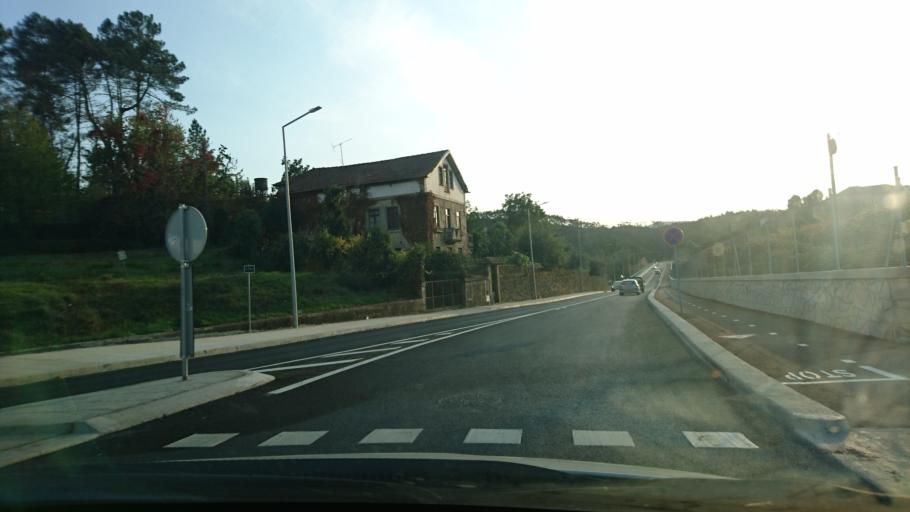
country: PT
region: Vila Real
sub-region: Mondim de Basto
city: Mondim de Basto
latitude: 41.4112
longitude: -7.9627
